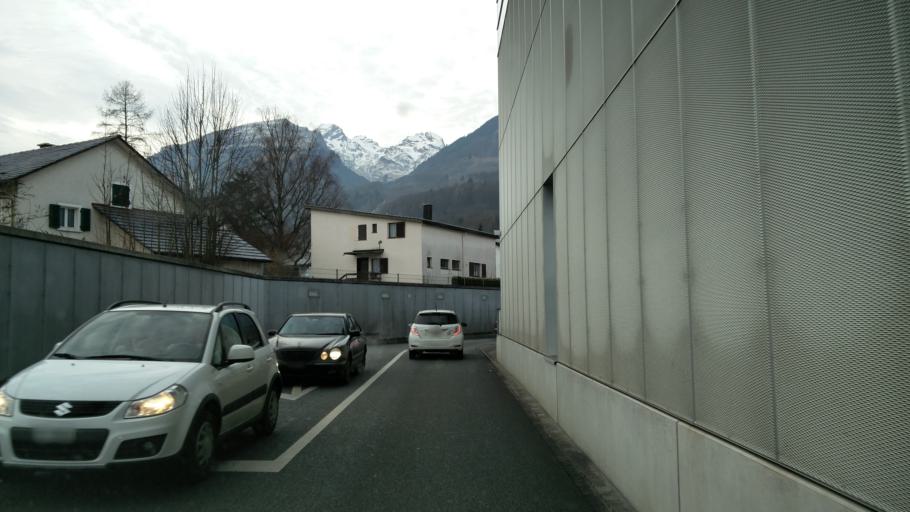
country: CH
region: Saint Gallen
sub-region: Wahlkreis Werdenberg
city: Buchs
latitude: 47.1639
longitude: 9.4731
